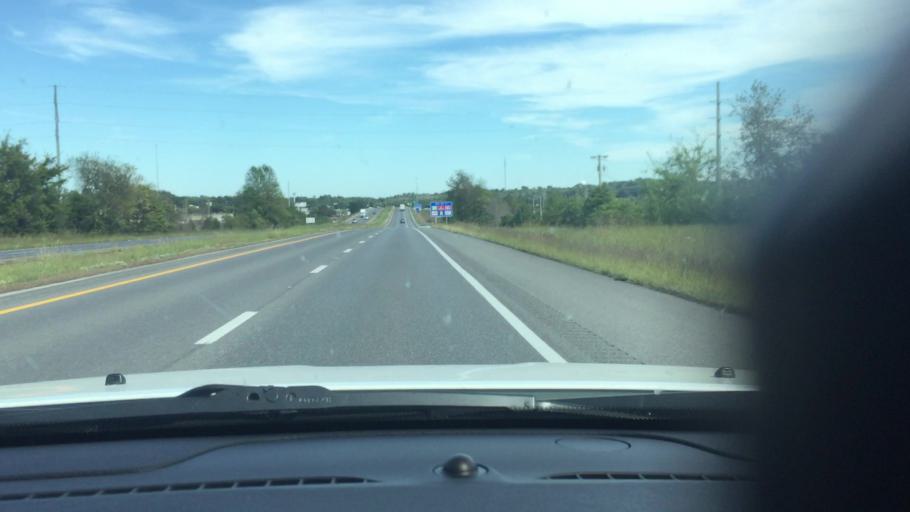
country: US
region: Kentucky
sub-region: Caldwell County
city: Princeton
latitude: 37.1194
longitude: -87.9084
